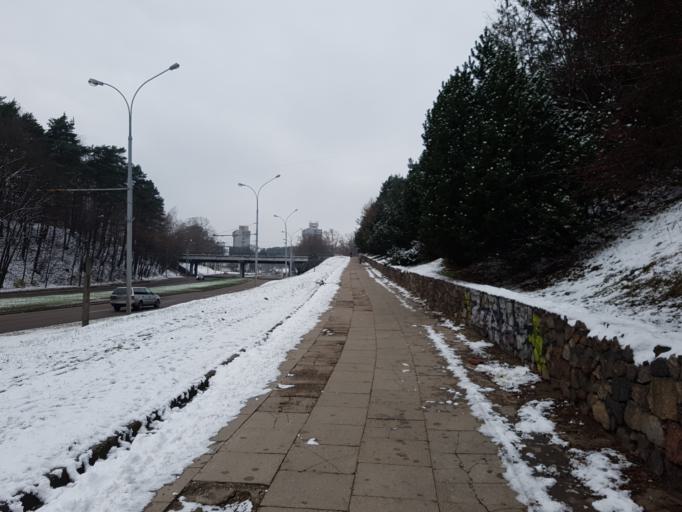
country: LT
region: Vilnius County
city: Lazdynai
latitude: 54.6779
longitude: 25.2197
